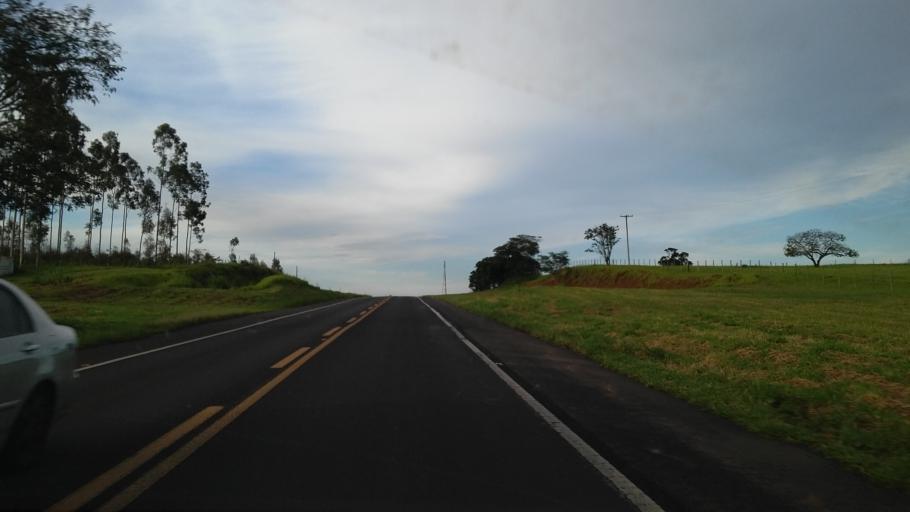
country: BR
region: Sao Paulo
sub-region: Lins
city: Lins
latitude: -21.9076
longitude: -49.9138
